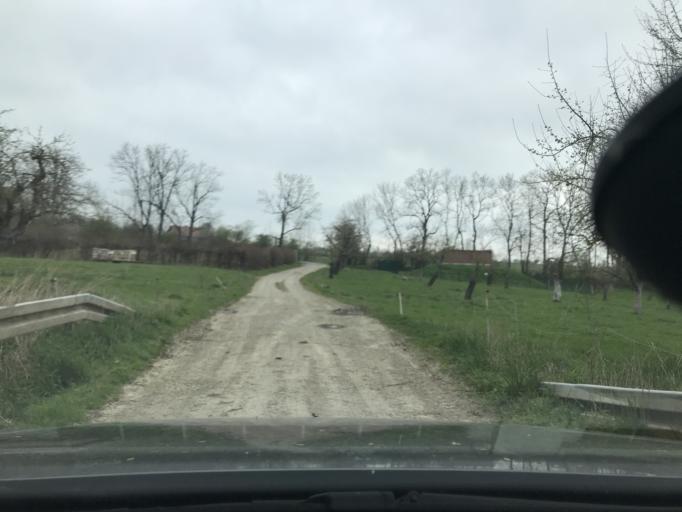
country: DE
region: Thuringia
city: Muehlhausen
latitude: 51.2229
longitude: 10.4246
